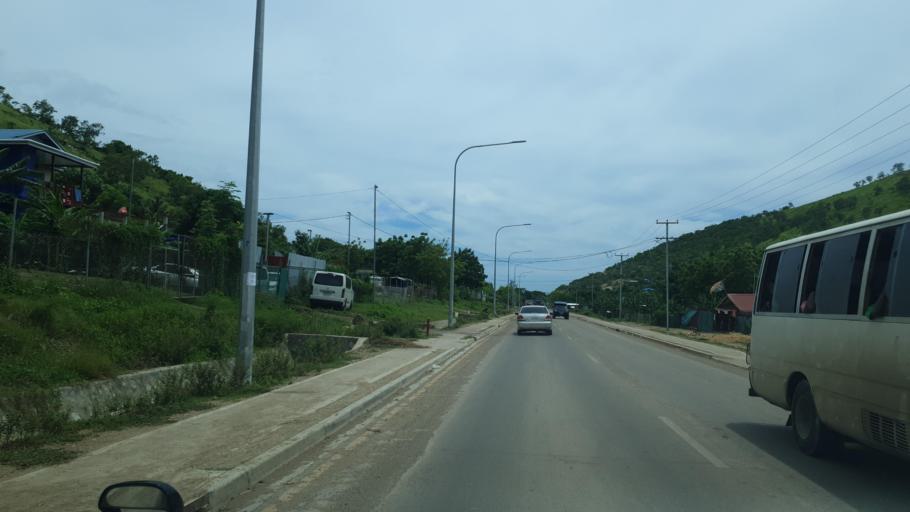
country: PG
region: National Capital
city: Port Moresby
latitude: -9.5262
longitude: 147.2415
